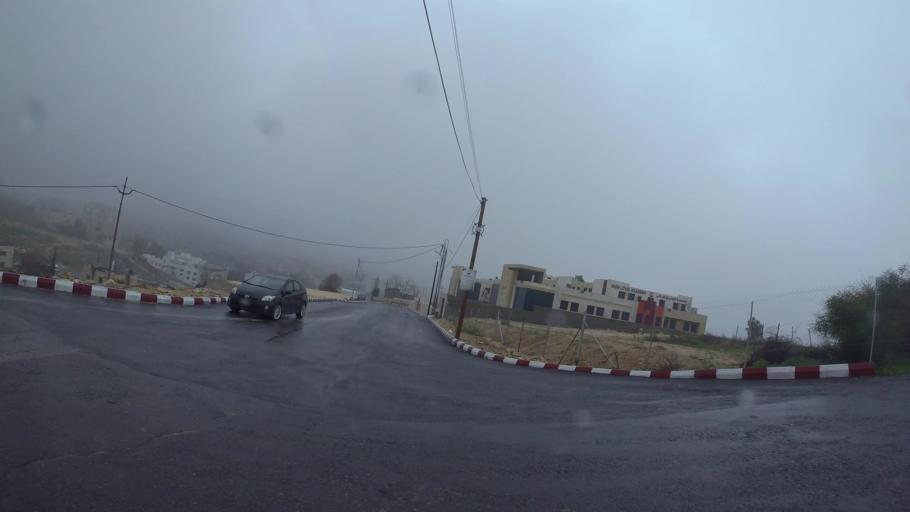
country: JO
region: Amman
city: Al Jubayhah
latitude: 32.0139
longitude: 35.8381
